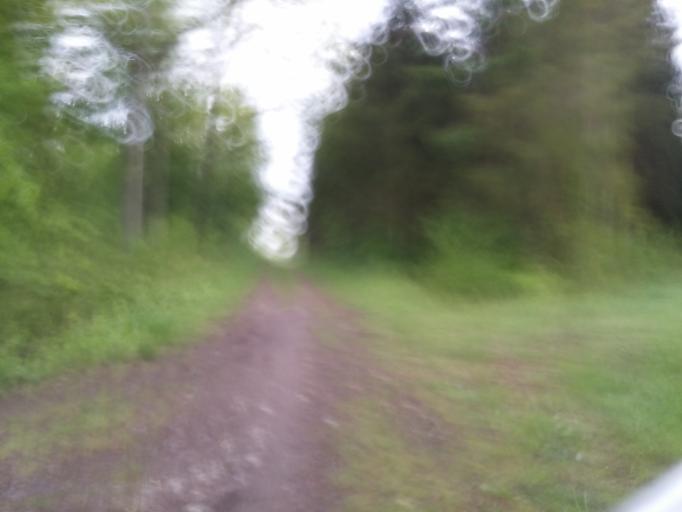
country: DK
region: South Denmark
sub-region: Kerteminde Kommune
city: Munkebo
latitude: 55.4269
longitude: 10.5505
